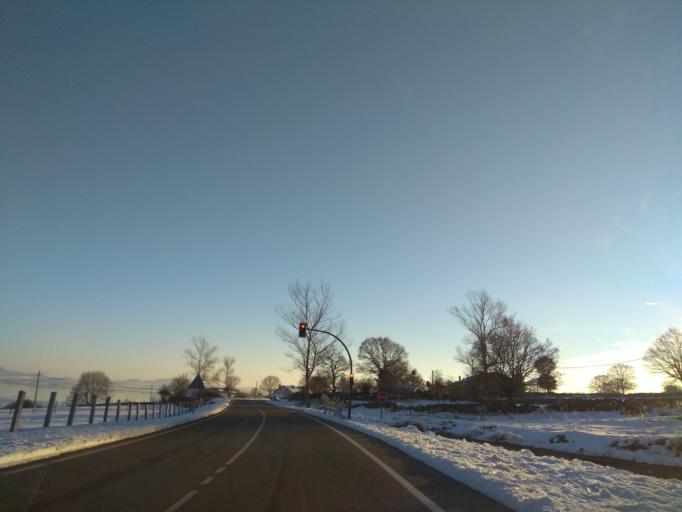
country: ES
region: Castille and Leon
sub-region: Provincia de Burgos
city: Arija
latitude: 43.0335
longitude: -3.9409
